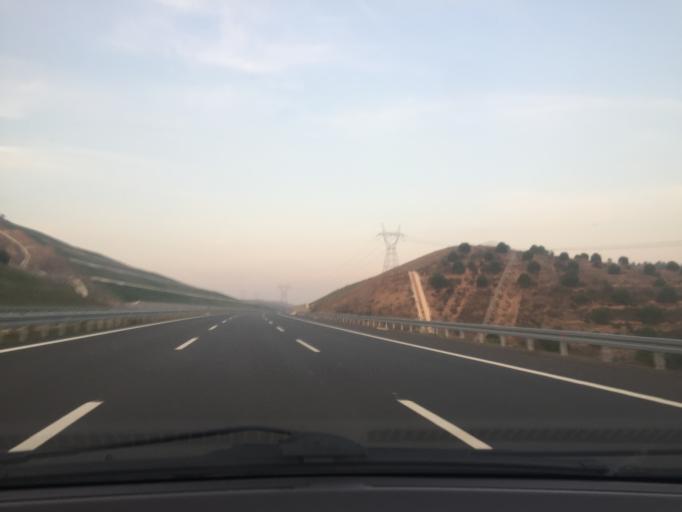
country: TR
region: Bursa
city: Mahmudiye
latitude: 40.2741
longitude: 28.5583
